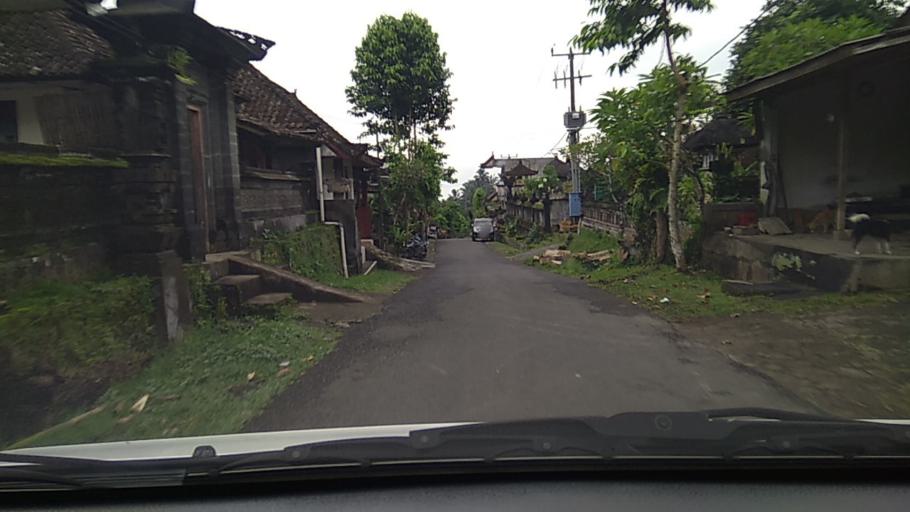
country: ID
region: Bali
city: Banjar Dujung Kaja
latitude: -8.4163
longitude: 115.2826
